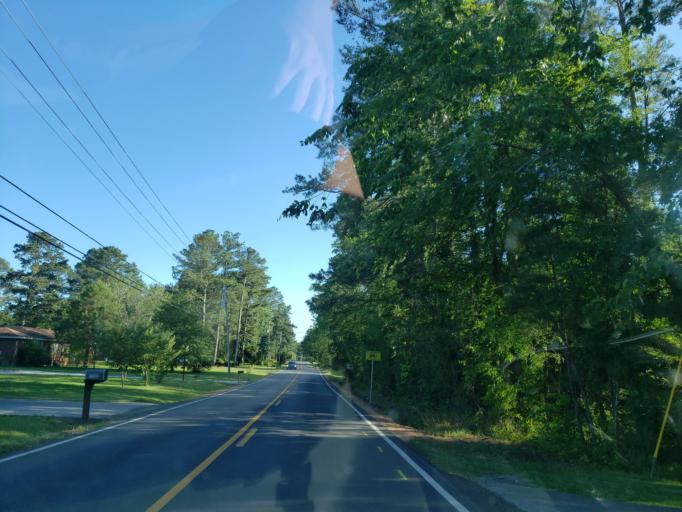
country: US
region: Georgia
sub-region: Floyd County
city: Rome
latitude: 34.3339
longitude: -85.1590
